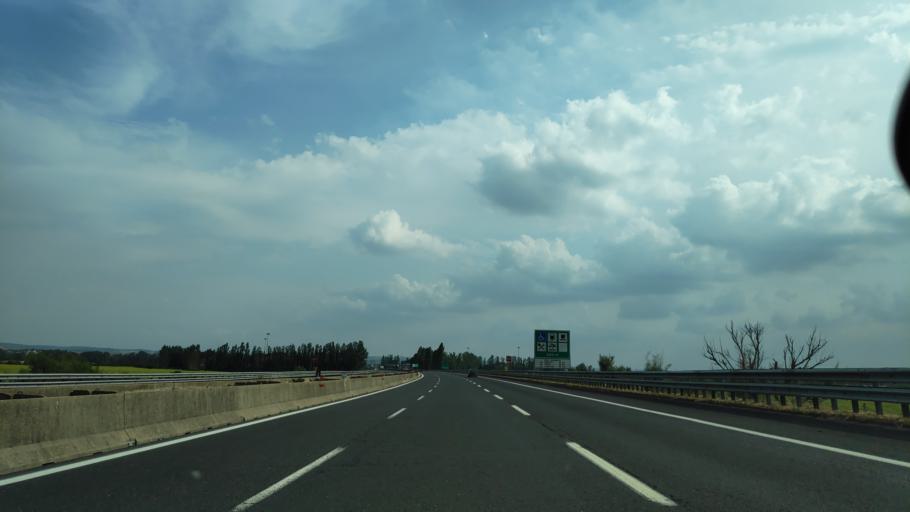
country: IT
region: Latium
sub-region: Citta metropolitana di Roma Capitale
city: Bivio di Capanelle
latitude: 42.1303
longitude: 12.6171
